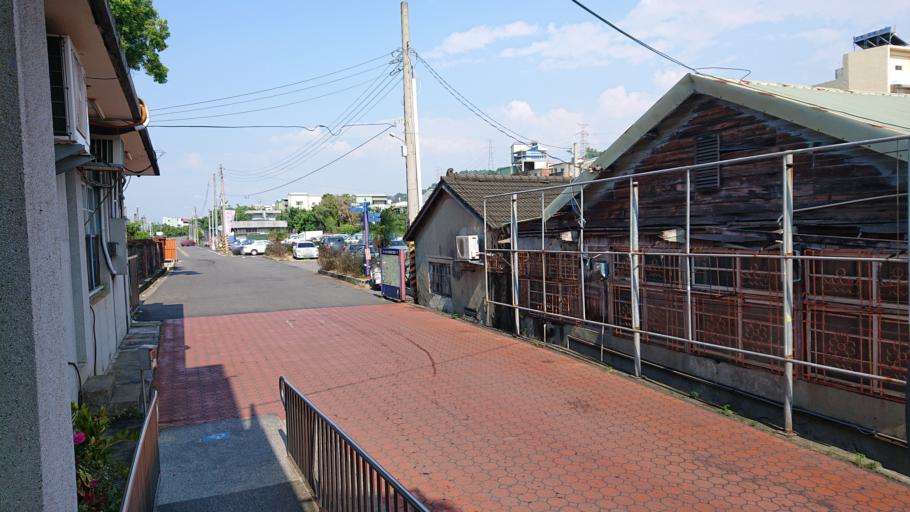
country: TW
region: Taiwan
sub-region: Yunlin
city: Douliu
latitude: 23.7597
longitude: 120.6150
